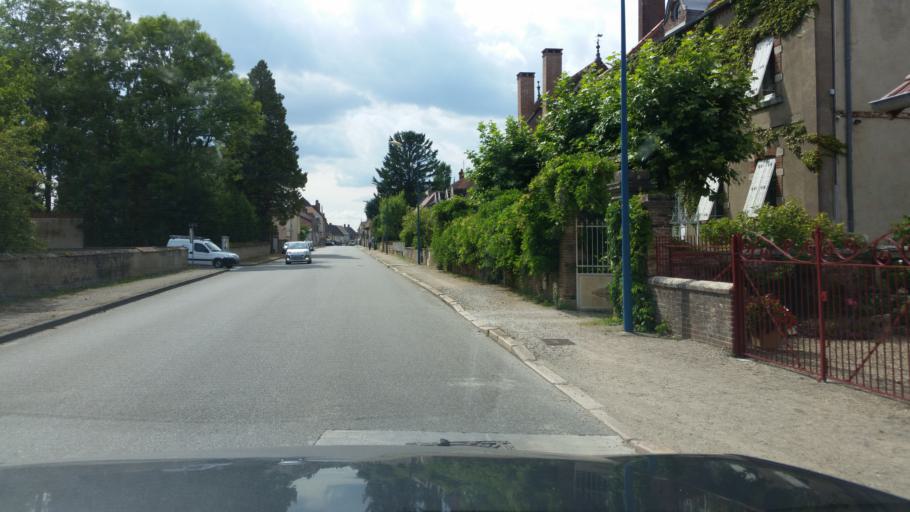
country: FR
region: Bourgogne
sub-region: Departement de Saone-et-Loire
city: Saint-Germain-du-Bois
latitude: 46.7524
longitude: 5.2476
